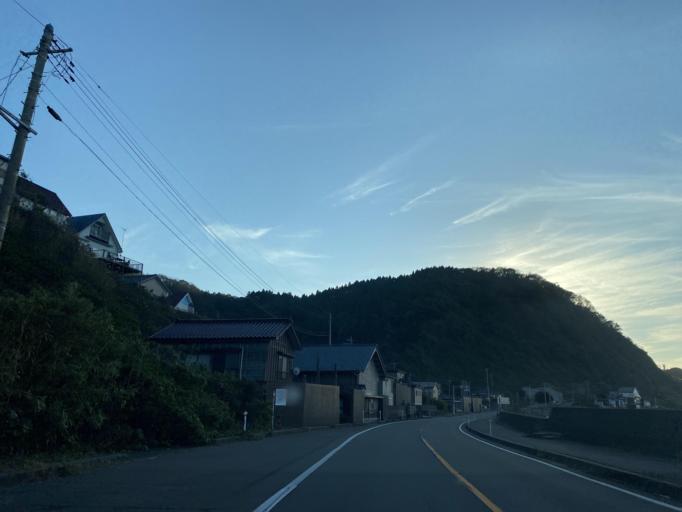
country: JP
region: Niigata
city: Kashiwazaki
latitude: 37.4858
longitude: 138.6283
